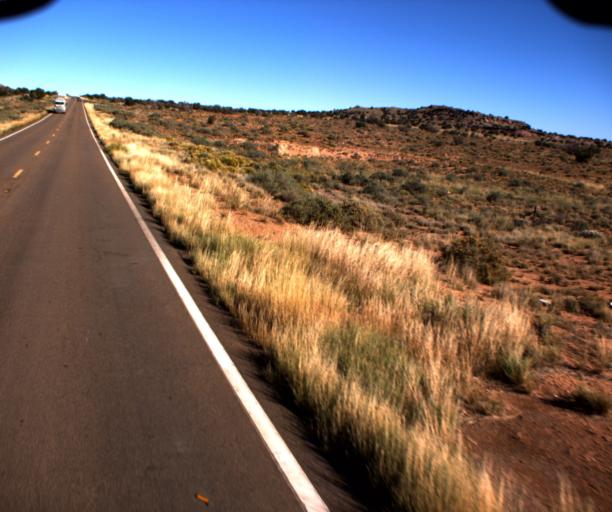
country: US
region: Arizona
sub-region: Navajo County
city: Snowflake
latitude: 34.6817
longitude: -110.1041
